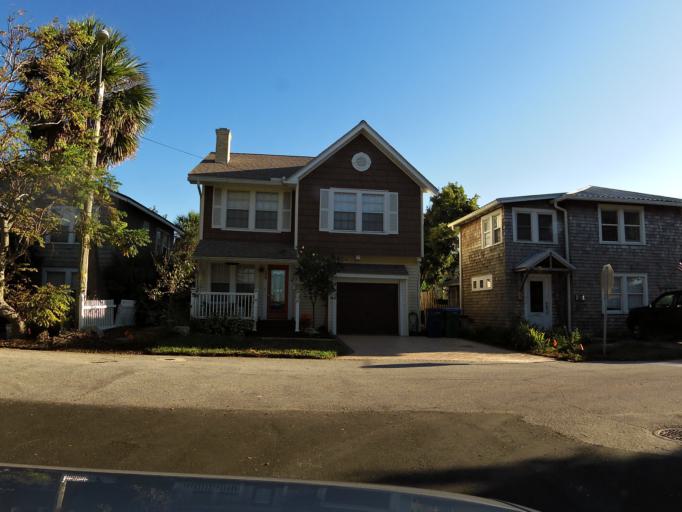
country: US
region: Florida
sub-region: Duval County
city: Neptune Beach
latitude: 30.3152
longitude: -81.3959
